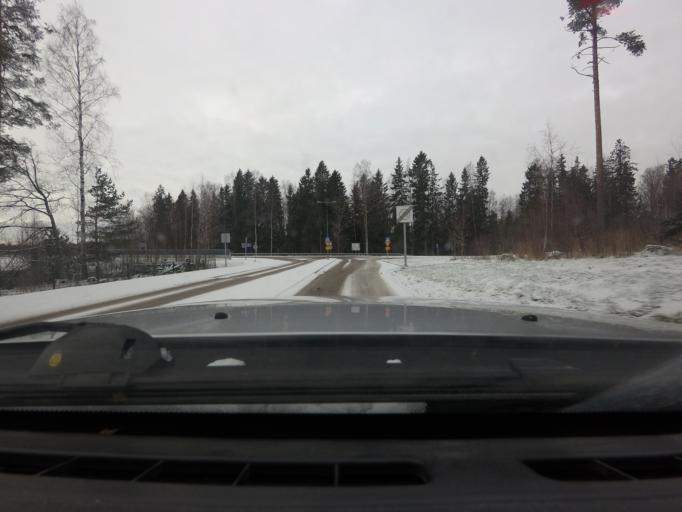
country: FI
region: Uusimaa
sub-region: Helsinki
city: Kilo
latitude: 60.2182
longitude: 24.7669
